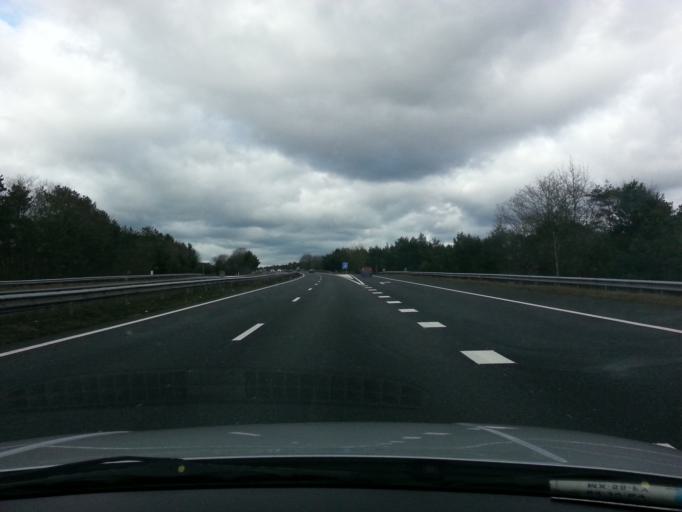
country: NL
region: Gelderland
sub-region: Gemeente Nunspeet
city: Nunspeet
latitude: 52.3722
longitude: 5.8191
